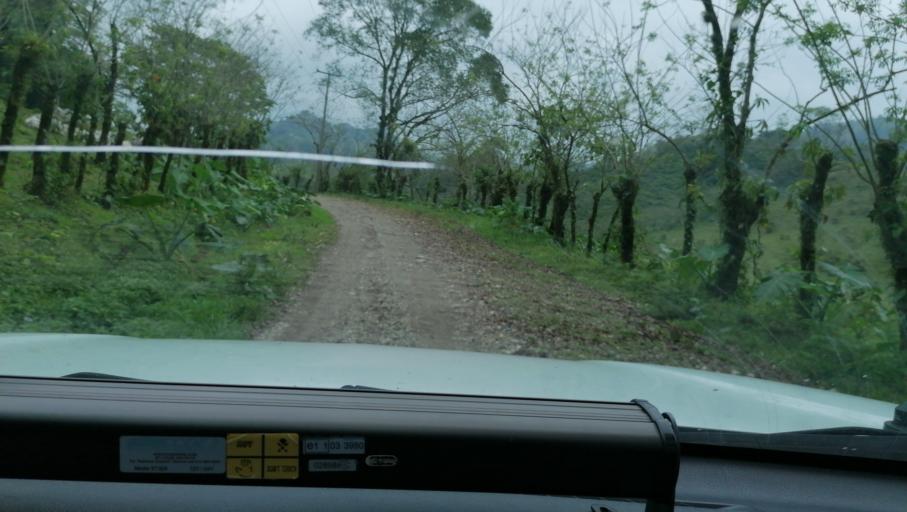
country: MX
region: Chiapas
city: Ixtacomitan
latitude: 17.3552
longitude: -93.1654
